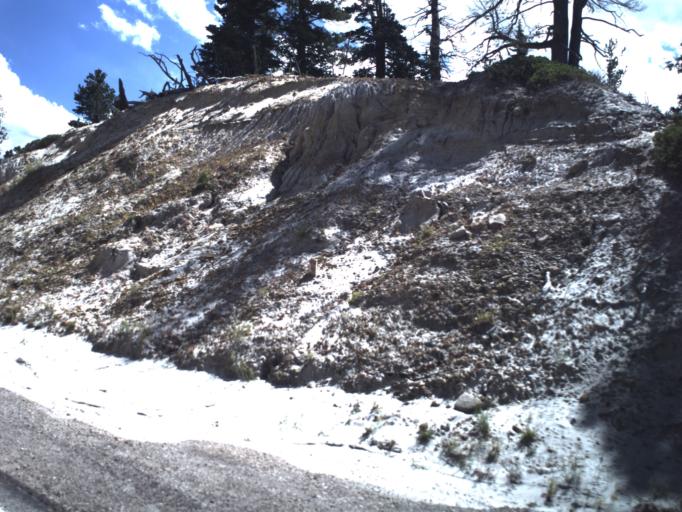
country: US
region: Utah
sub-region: Iron County
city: Cedar City
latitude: 37.5816
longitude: -112.8816
